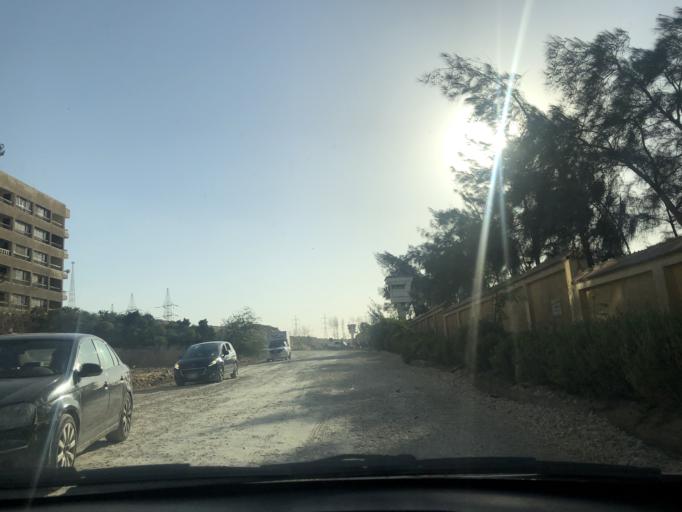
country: EG
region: Al Jizah
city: Al Jizah
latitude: 29.9919
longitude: 31.1113
